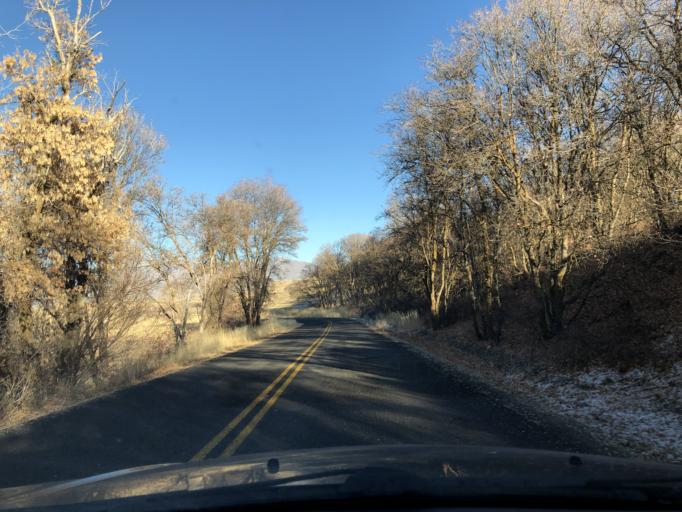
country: US
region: Utah
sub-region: Cache County
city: Wellsville
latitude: 41.5777
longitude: -111.9217
